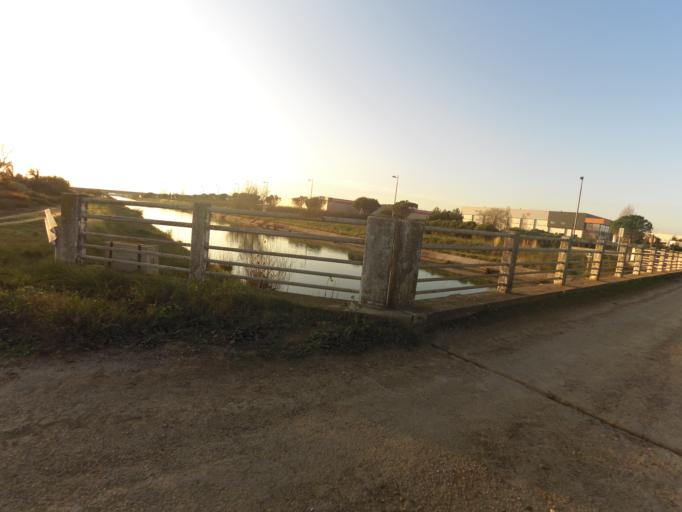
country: FR
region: Languedoc-Roussillon
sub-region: Departement du Gard
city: Aigues-Vives
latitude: 43.7185
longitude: 4.1882
